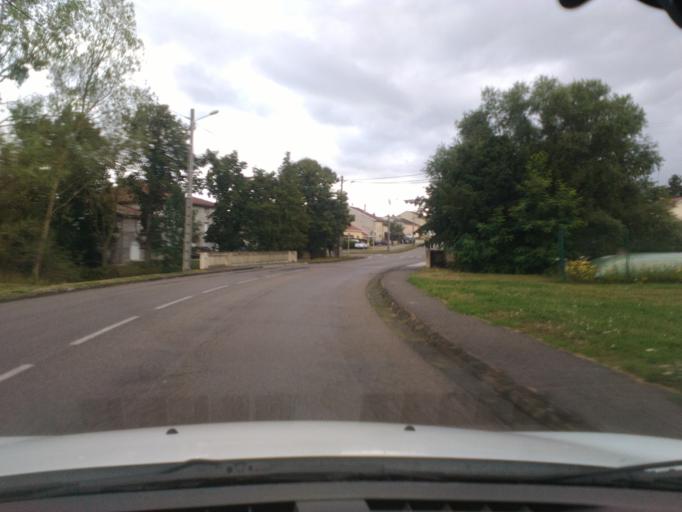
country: FR
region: Lorraine
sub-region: Departement des Vosges
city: Mirecourt
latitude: 48.3931
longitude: 6.1334
